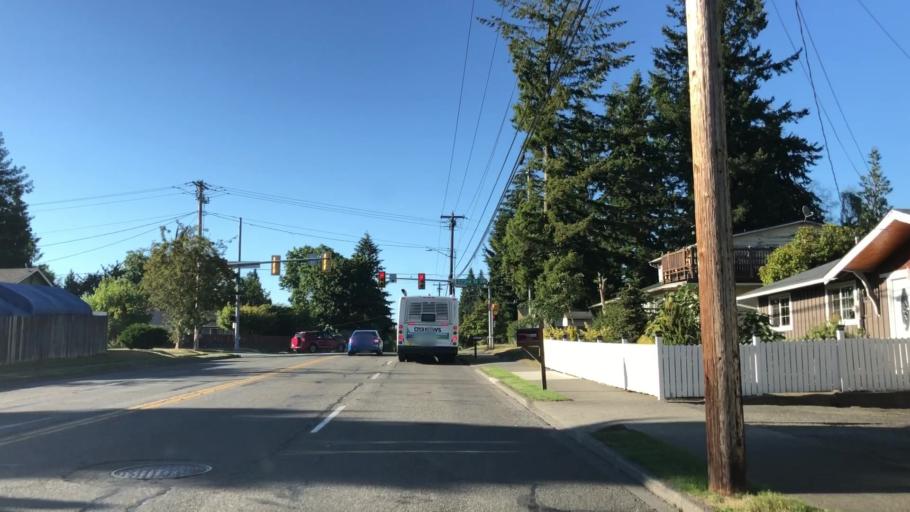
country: US
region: Washington
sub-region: Snohomish County
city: Mountlake Terrace
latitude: 47.7964
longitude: -122.2923
